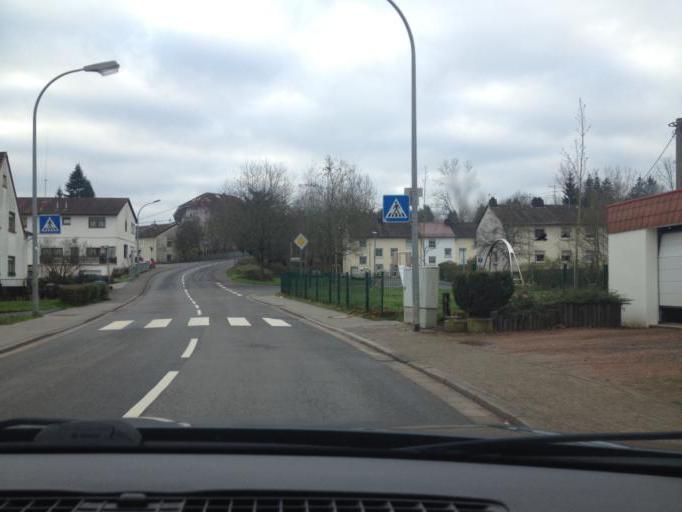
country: DE
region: Saarland
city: Neunkirchen
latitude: 49.3701
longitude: 7.1734
